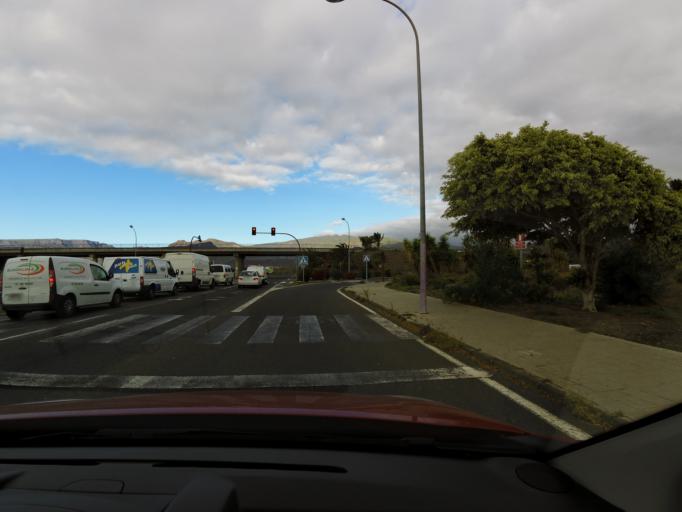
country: ES
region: Canary Islands
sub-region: Provincia de Las Palmas
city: Cruce de Arinaga
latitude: 27.8696
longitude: -15.4284
